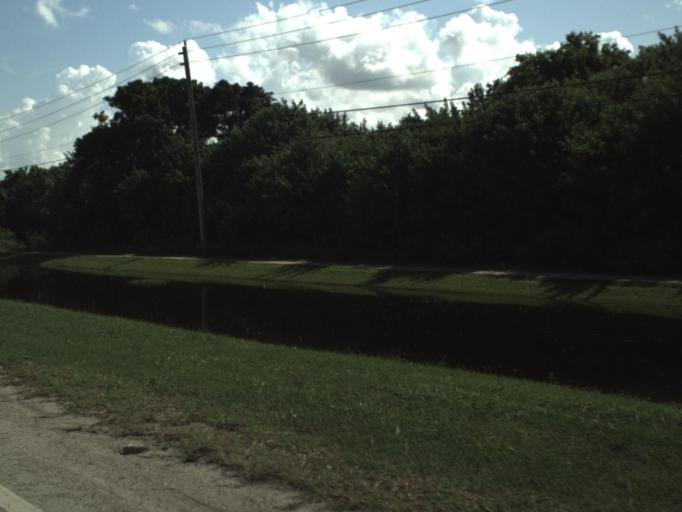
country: US
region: Florida
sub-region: Palm Beach County
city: Villages of Oriole
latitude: 26.5331
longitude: -80.2056
